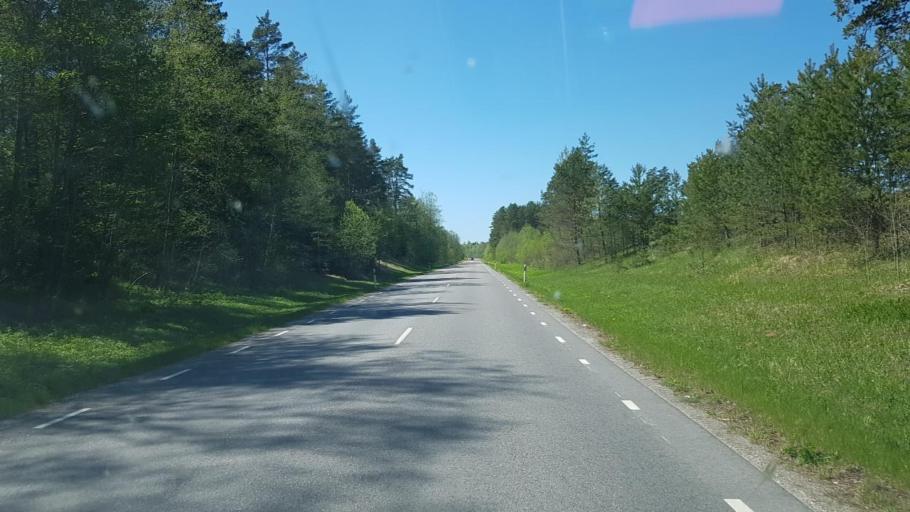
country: EE
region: Ida-Virumaa
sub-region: Narva-Joesuu linn
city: Narva-Joesuu
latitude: 59.4139
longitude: 28.0845
